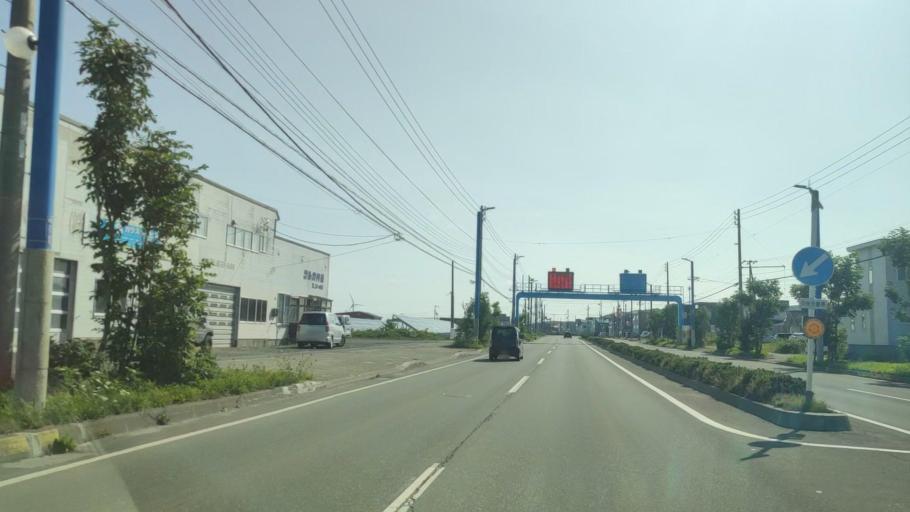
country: JP
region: Hokkaido
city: Wakkanai
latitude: 45.3949
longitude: 141.7150
